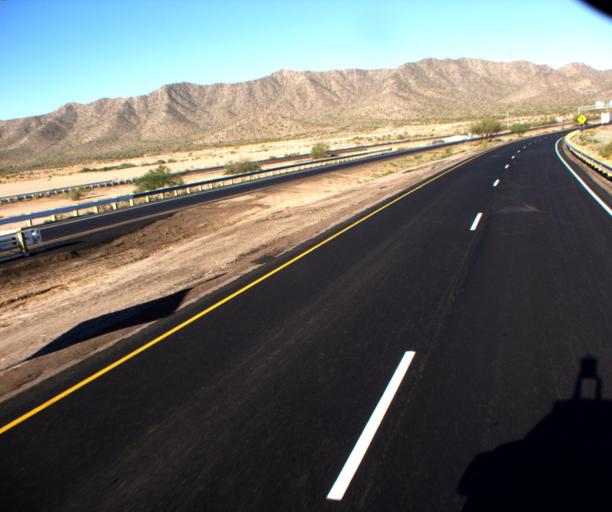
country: US
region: Arizona
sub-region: Pinal County
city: Arizona City
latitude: 32.8195
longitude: -111.6849
